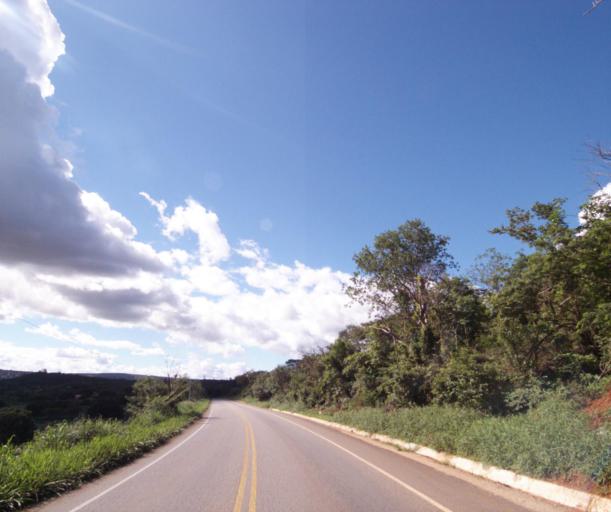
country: BR
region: Bahia
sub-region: Caetite
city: Caetite
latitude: -14.0733
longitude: -42.4577
